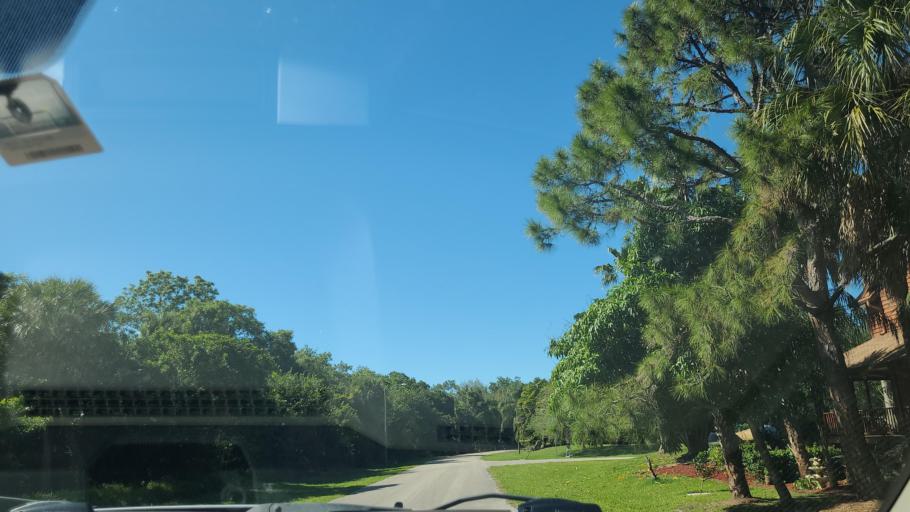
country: US
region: Florida
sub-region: Indian River County
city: Sebastian
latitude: 27.7639
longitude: -80.5017
